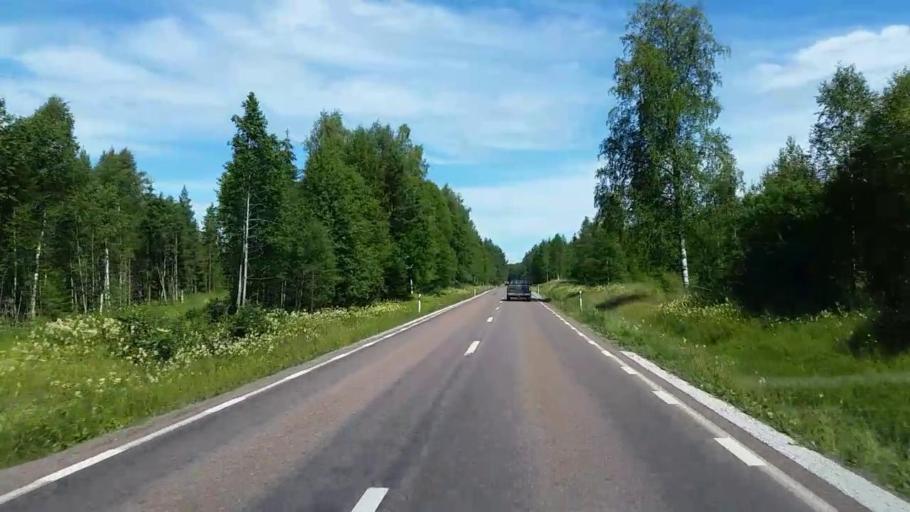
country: SE
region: Dalarna
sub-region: Rattviks Kommun
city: Raettvik
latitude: 60.9037
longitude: 15.1891
